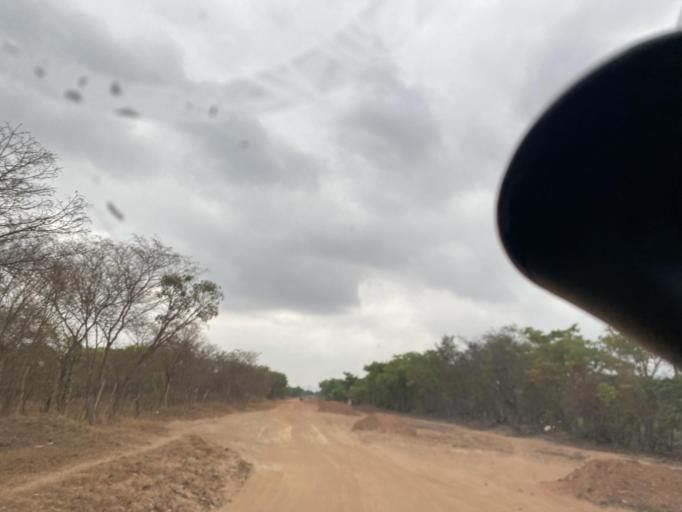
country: ZM
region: Lusaka
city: Chongwe
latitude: -15.2655
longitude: 28.7319
